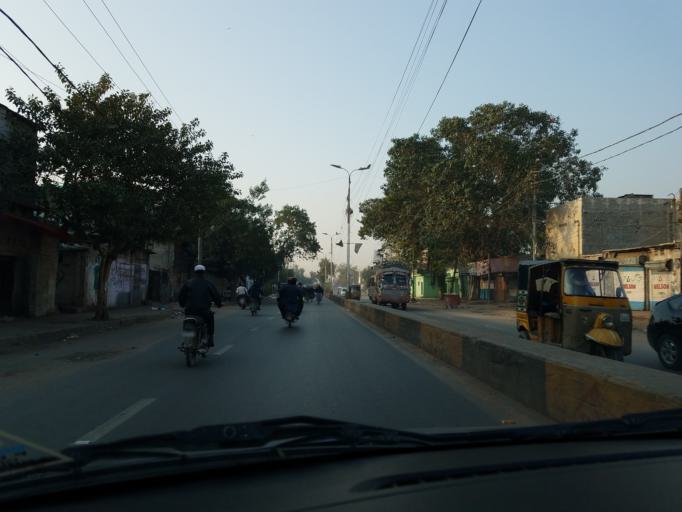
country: PK
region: Sindh
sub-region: Karachi District
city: Karachi
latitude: 24.8903
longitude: 67.0429
